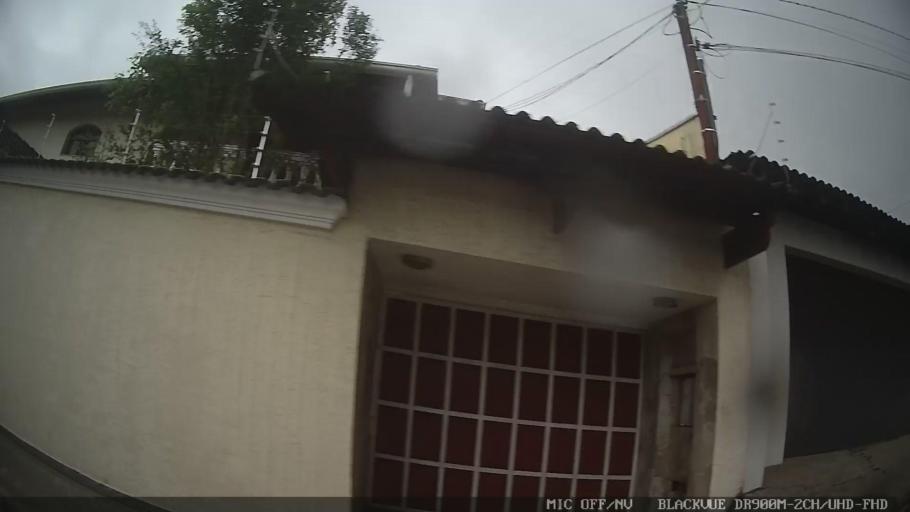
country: BR
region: Sao Paulo
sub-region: Mogi das Cruzes
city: Mogi das Cruzes
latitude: -23.5298
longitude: -46.1792
